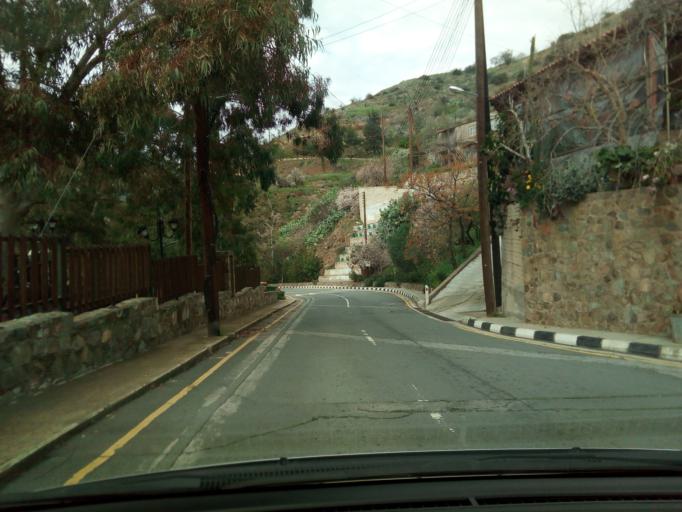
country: CY
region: Lefkosia
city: Klirou
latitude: 34.9582
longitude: 33.1579
